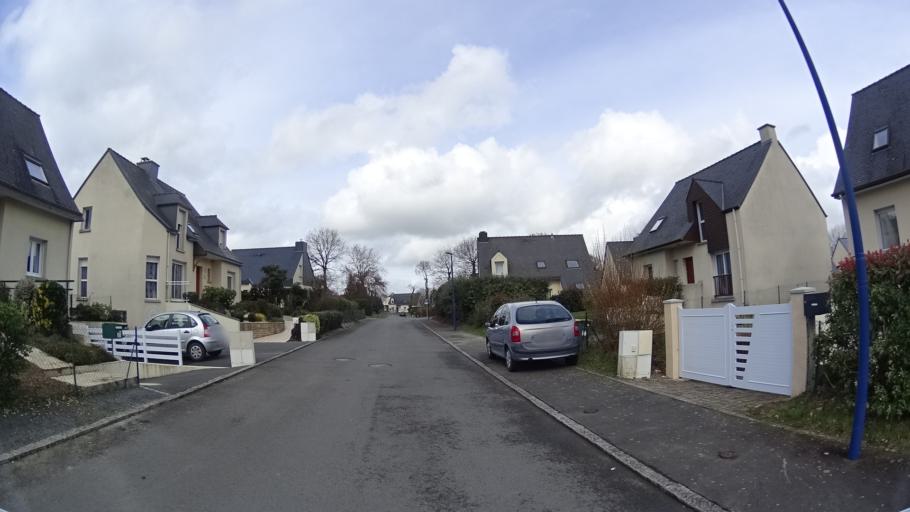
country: FR
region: Brittany
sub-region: Departement d'Ille-et-Vilaine
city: Saint-Gilles
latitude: 48.1515
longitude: -1.8351
